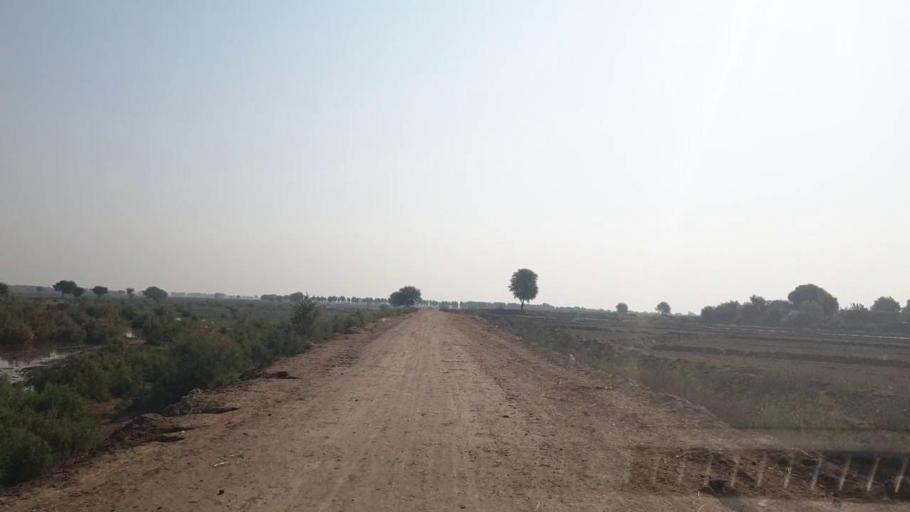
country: PK
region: Sindh
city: Sehwan
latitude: 26.4519
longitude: 67.8311
